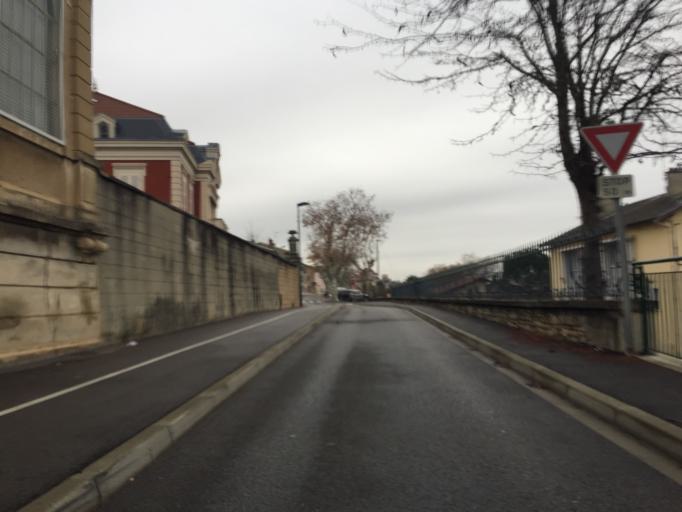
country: FR
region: Rhone-Alpes
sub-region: Departement de l'Ain
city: Miribel
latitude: 45.8221
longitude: 4.9525
